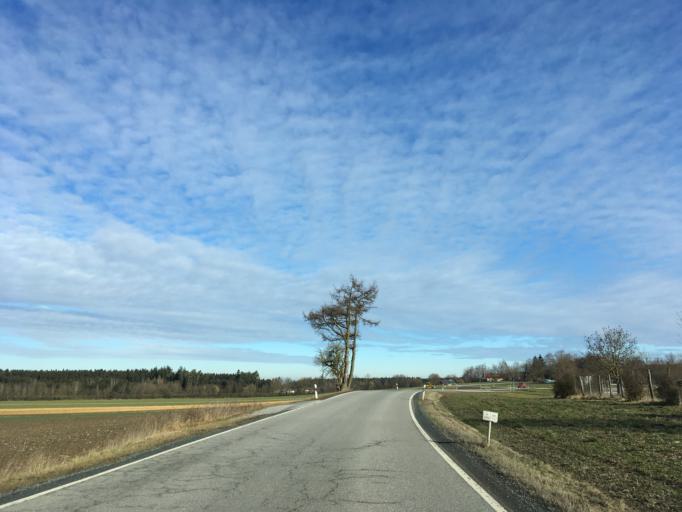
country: DE
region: Bavaria
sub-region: Upper Bavaria
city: Unterreit
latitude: 48.1136
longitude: 12.3178
